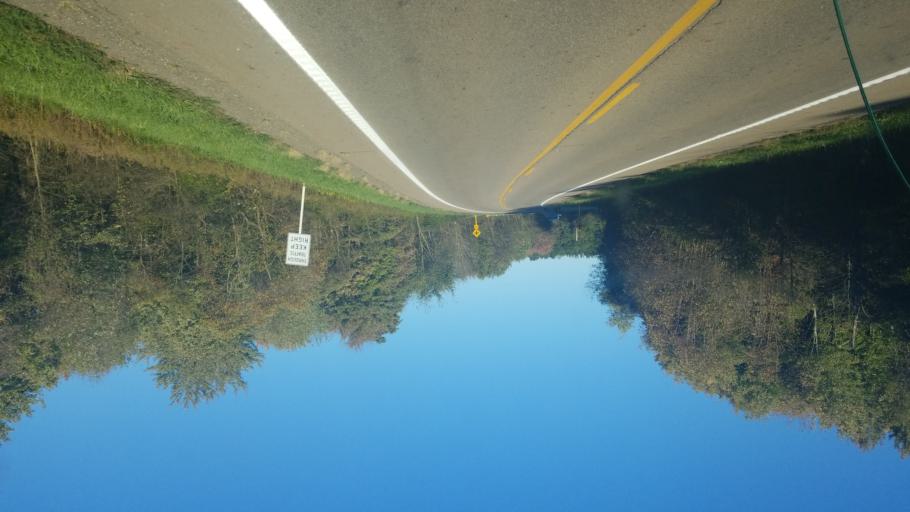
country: US
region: Ohio
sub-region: Columbiana County
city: Glenmoor
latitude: 40.6867
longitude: -80.6313
